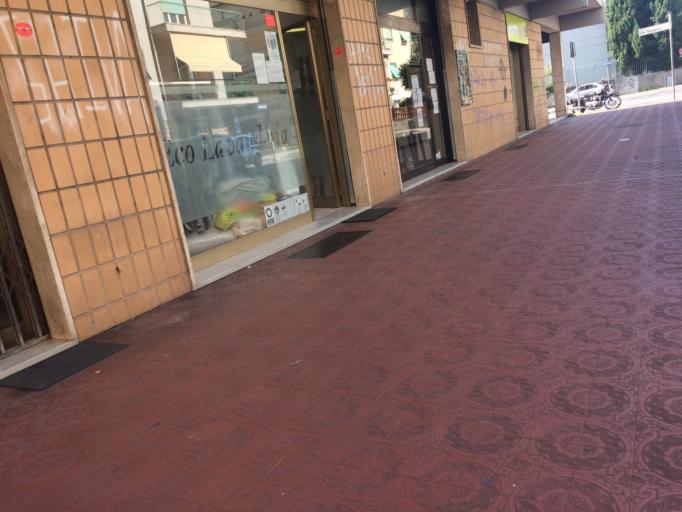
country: IT
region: Tuscany
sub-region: Provincia di Massa-Carrara
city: Massa
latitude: 44.0347
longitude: 10.1357
